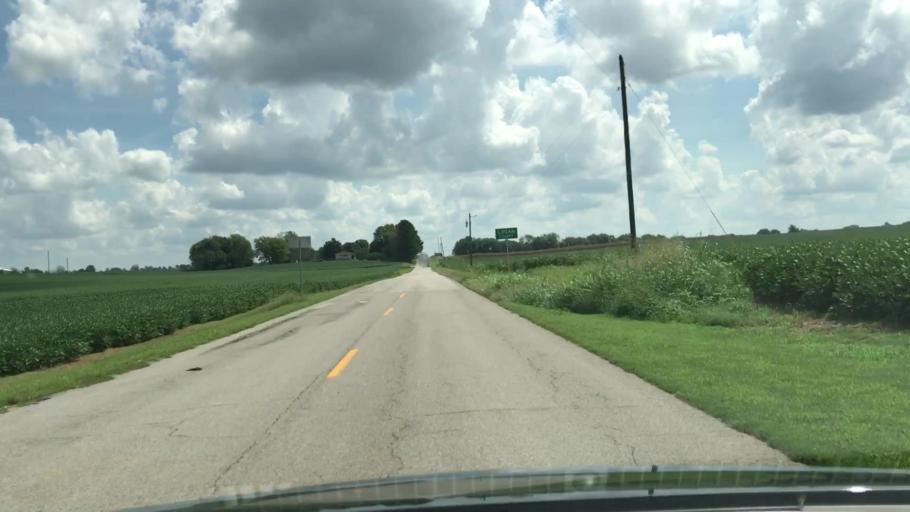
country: US
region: Kentucky
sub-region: Todd County
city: Guthrie
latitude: 36.7133
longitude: -87.0606
